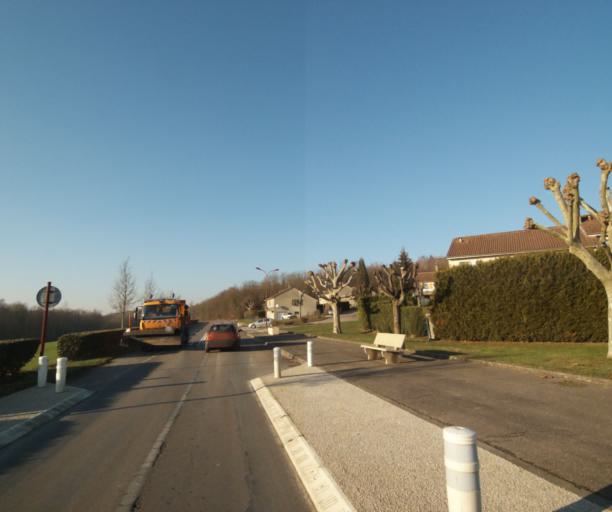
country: FR
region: Champagne-Ardenne
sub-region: Departement de la Haute-Marne
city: Bienville
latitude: 48.5586
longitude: 5.0712
